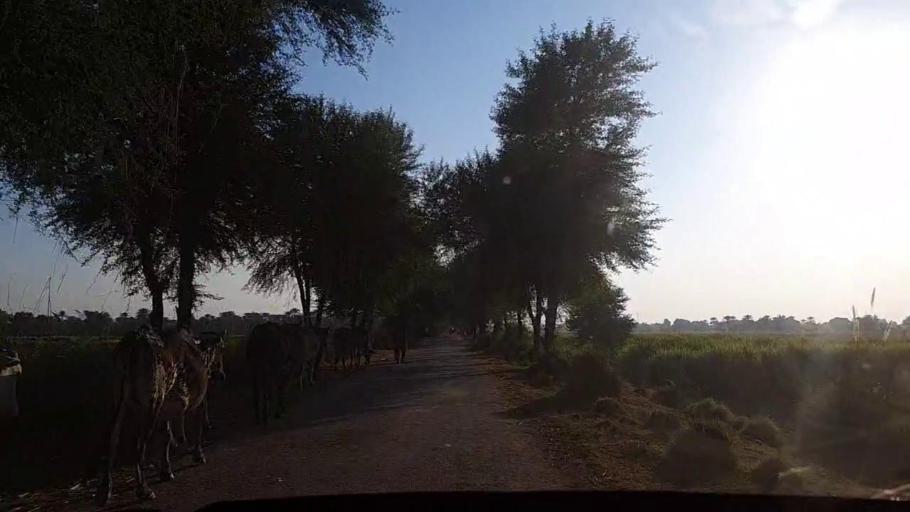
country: PK
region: Sindh
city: Sobhadero
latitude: 27.4062
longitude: 68.3921
